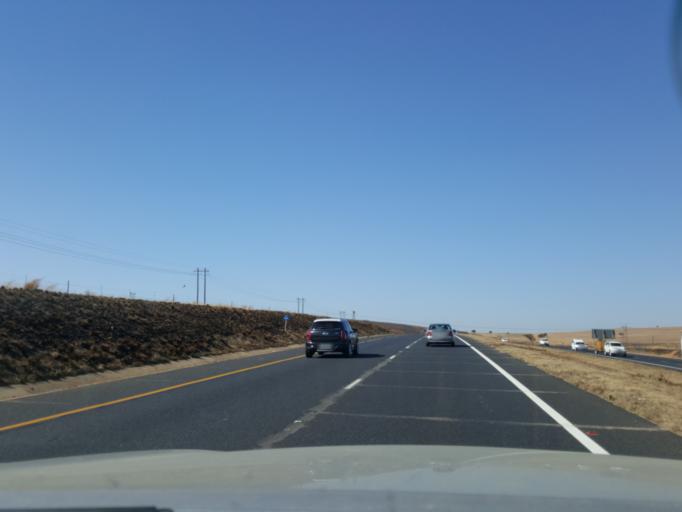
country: ZA
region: Mpumalanga
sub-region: Nkangala District Municipality
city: Witbank
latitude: -25.8786
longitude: 29.3133
